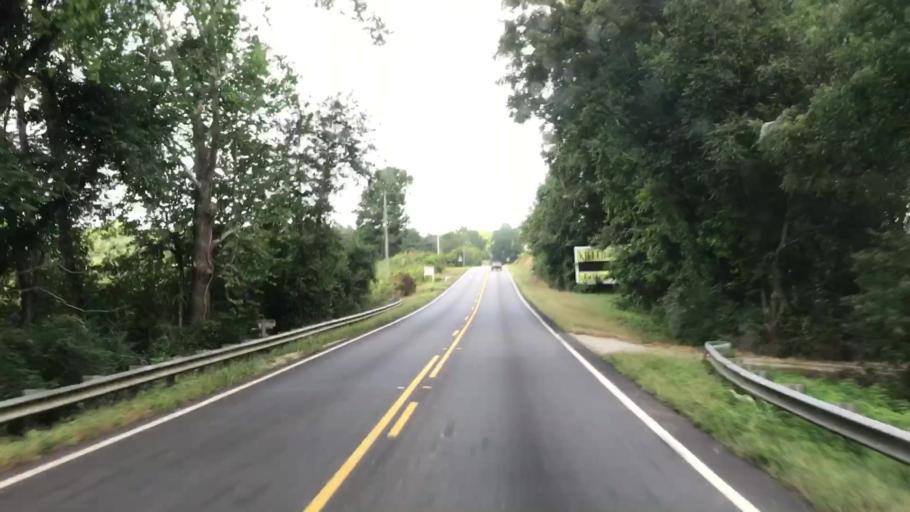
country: US
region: Georgia
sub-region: Greene County
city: Greensboro
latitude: 33.5692
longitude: -83.1633
